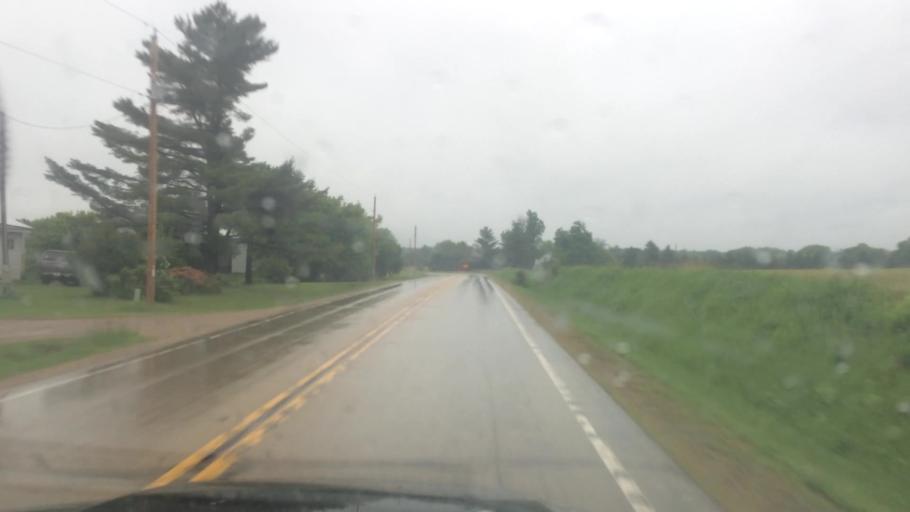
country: US
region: Wisconsin
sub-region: Waupaca County
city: Marion
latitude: 44.6102
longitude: -88.8836
